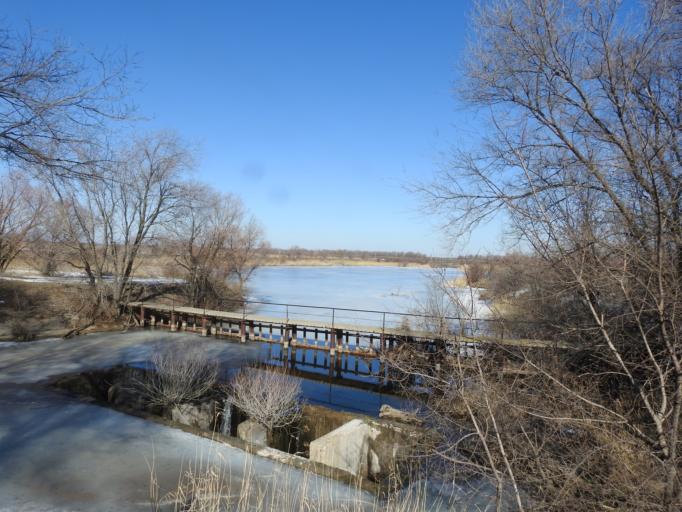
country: RU
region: Saratov
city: Yershov
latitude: 51.3728
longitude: 48.2403
